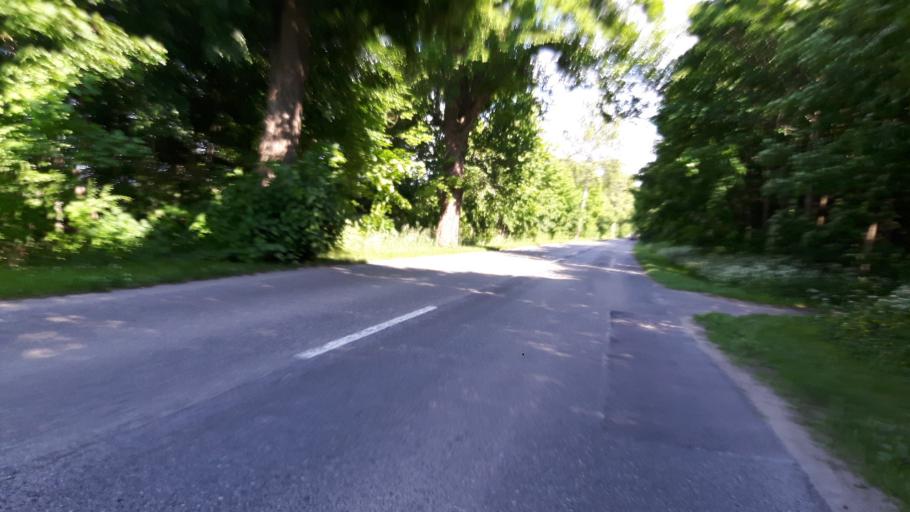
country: PL
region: Pomeranian Voivodeship
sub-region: Powiat wejherowski
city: Orle
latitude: 54.6458
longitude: 18.1175
